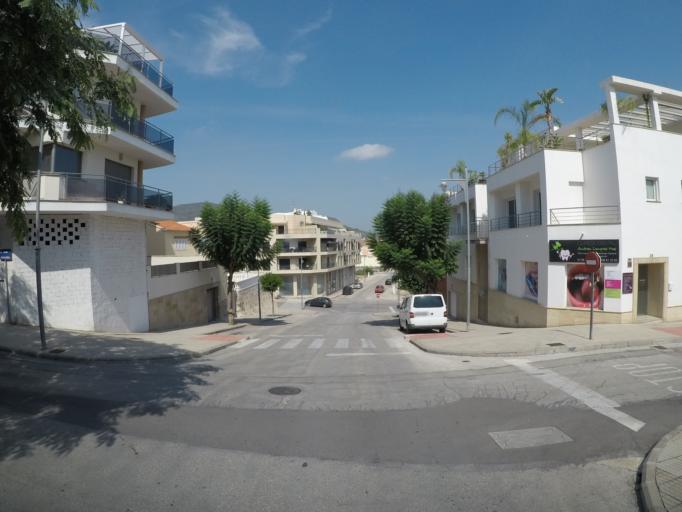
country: ES
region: Valencia
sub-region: Provincia de Alicante
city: Pego
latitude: 38.8424
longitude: -0.1131
